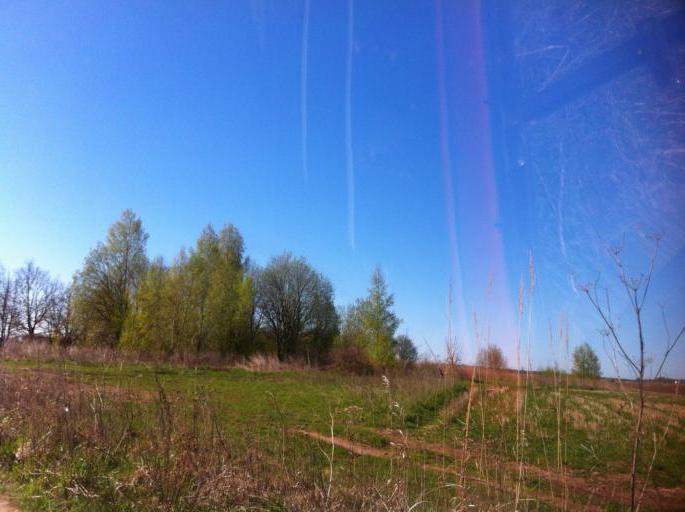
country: RU
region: Pskov
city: Izborsk
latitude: 57.7974
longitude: 27.9638
